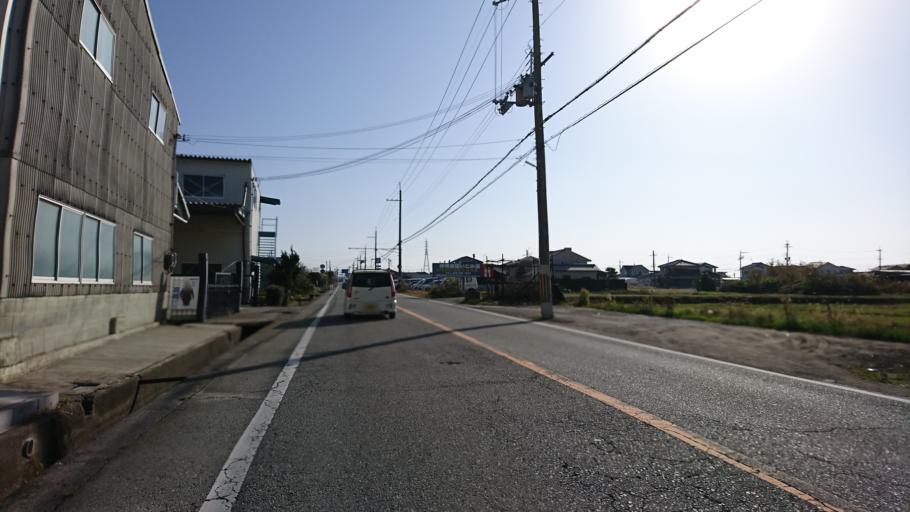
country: JP
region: Hyogo
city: Miki
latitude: 34.7609
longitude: 134.9477
